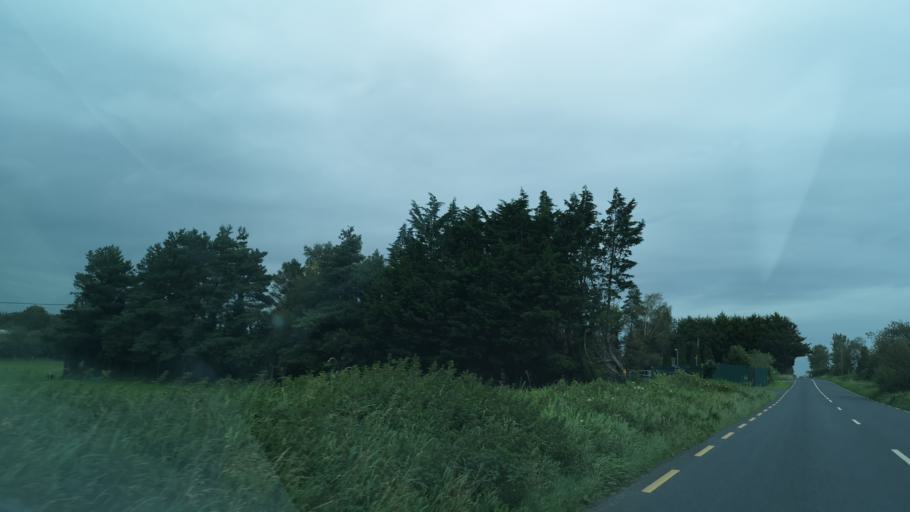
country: IE
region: Leinster
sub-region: Uibh Fhaili
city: Banagher
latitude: 53.2127
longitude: -7.9030
